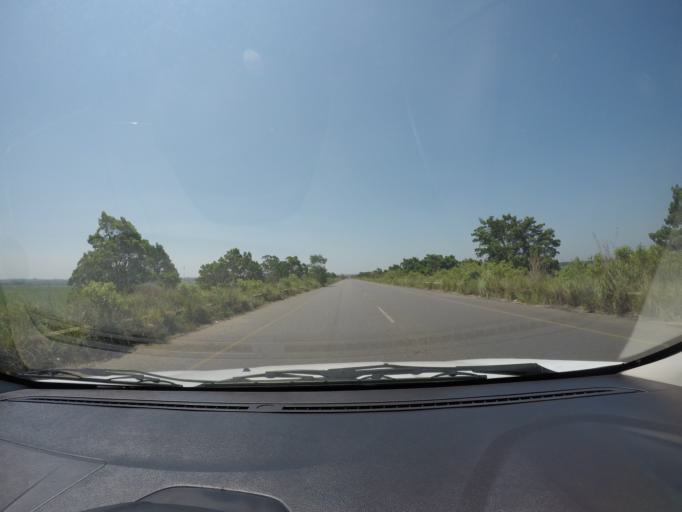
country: ZA
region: KwaZulu-Natal
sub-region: uThungulu District Municipality
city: Empangeni
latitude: -28.7907
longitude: 31.9581
